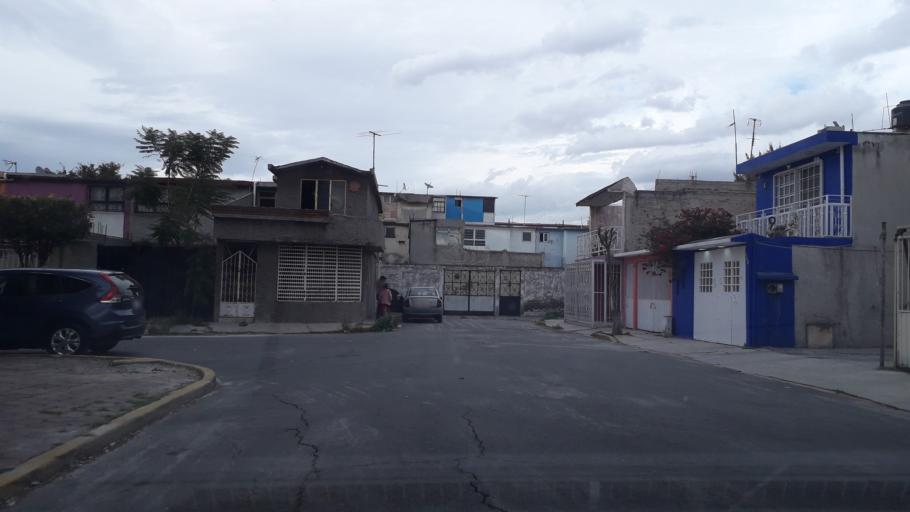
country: MX
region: Mexico
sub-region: Jaltenco
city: Alborada Jaltenco
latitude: 19.6598
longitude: -99.0675
